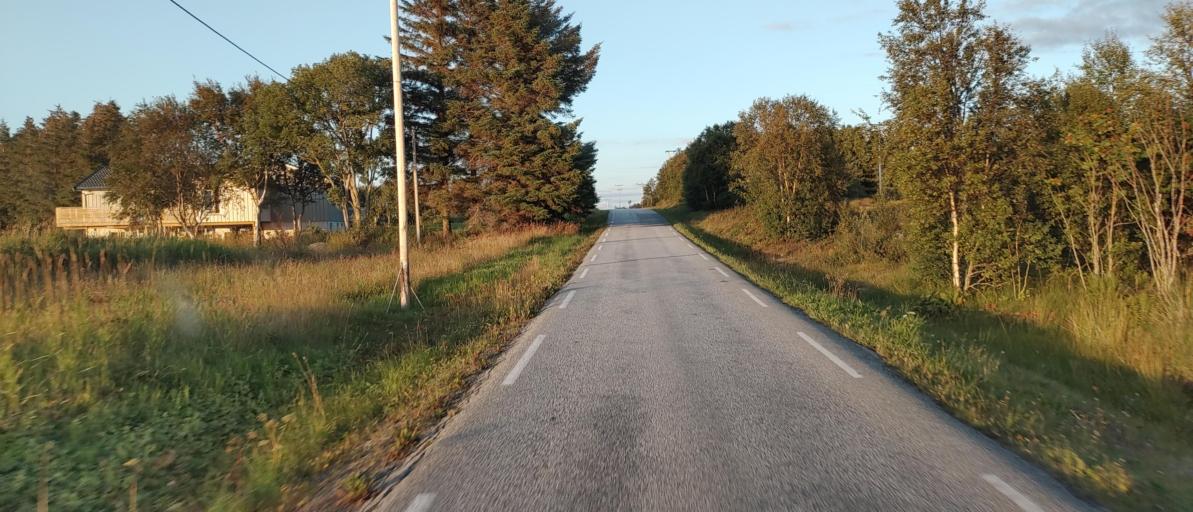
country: NO
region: More og Romsdal
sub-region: Fraena
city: Elnesvagen
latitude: 62.9987
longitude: 7.2353
